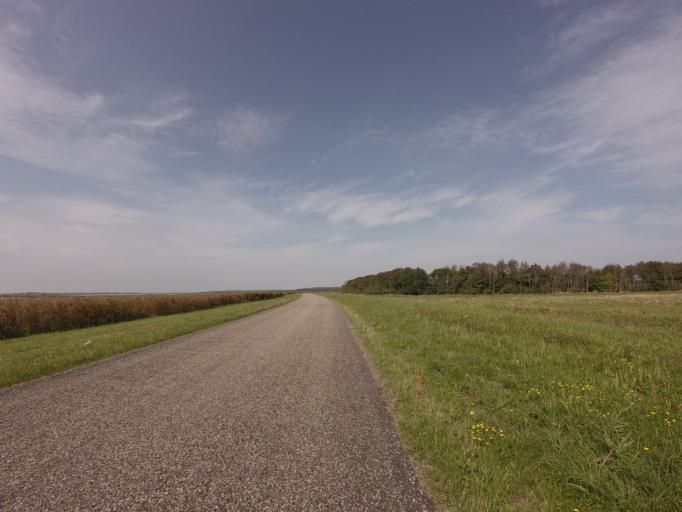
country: NL
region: Groningen
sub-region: Gemeente De Marne
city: Ulrum
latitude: 53.3558
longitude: 6.2640
